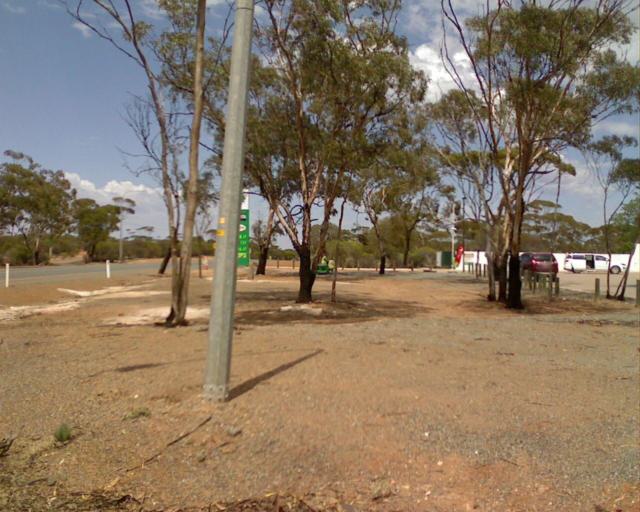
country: AU
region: Western Australia
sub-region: Kalgoorlie/Boulder
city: Stoneville
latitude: -31.1985
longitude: 121.6523
